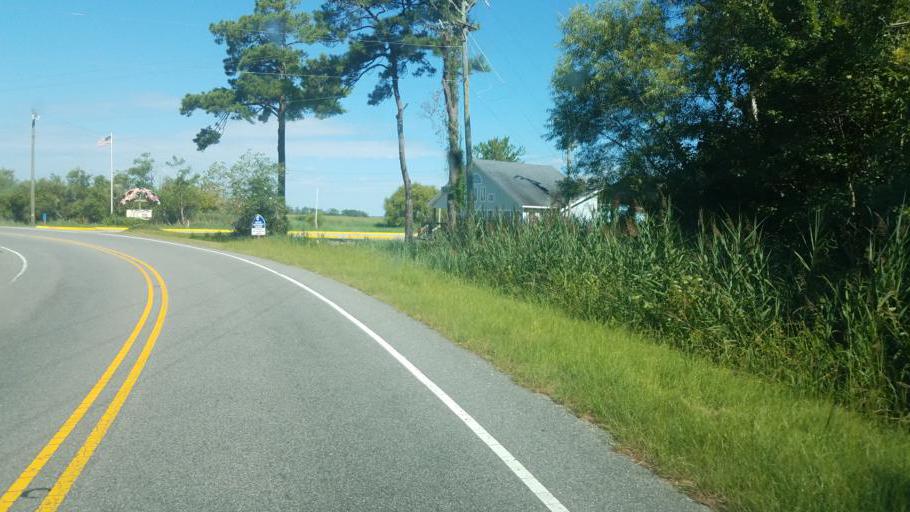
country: US
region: North Carolina
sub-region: Dare County
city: Kill Devil Hills
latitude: 36.0145
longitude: -75.6785
